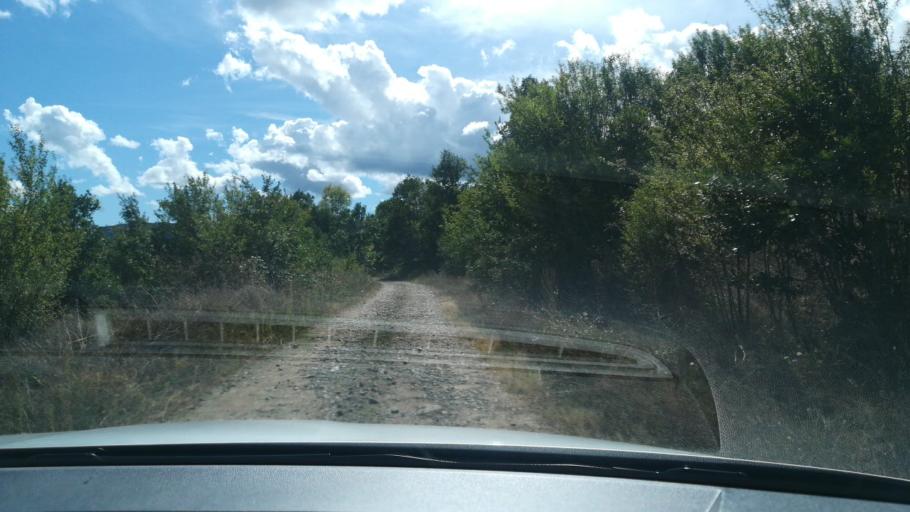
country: MK
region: Delcevo
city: Delcevo
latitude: 41.9000
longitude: 22.8055
